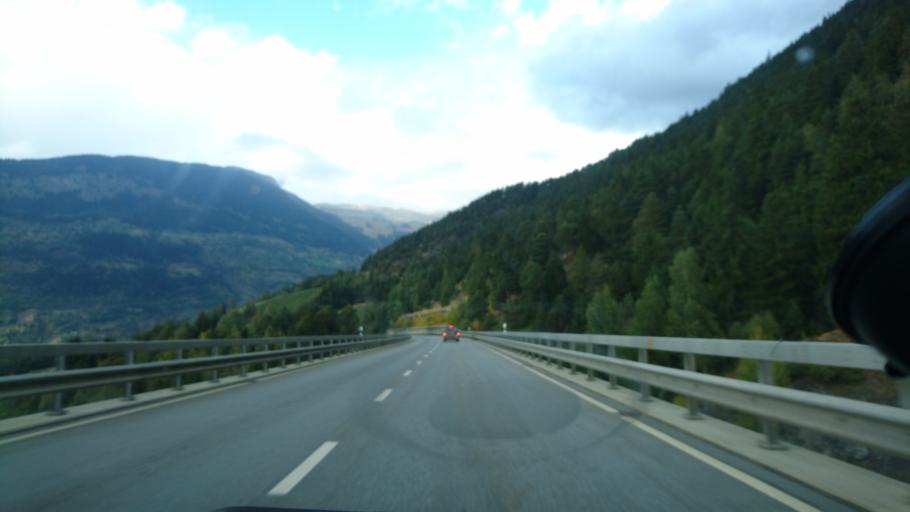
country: CH
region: Valais
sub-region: Brig District
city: Naters
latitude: 46.3230
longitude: 8.0333
